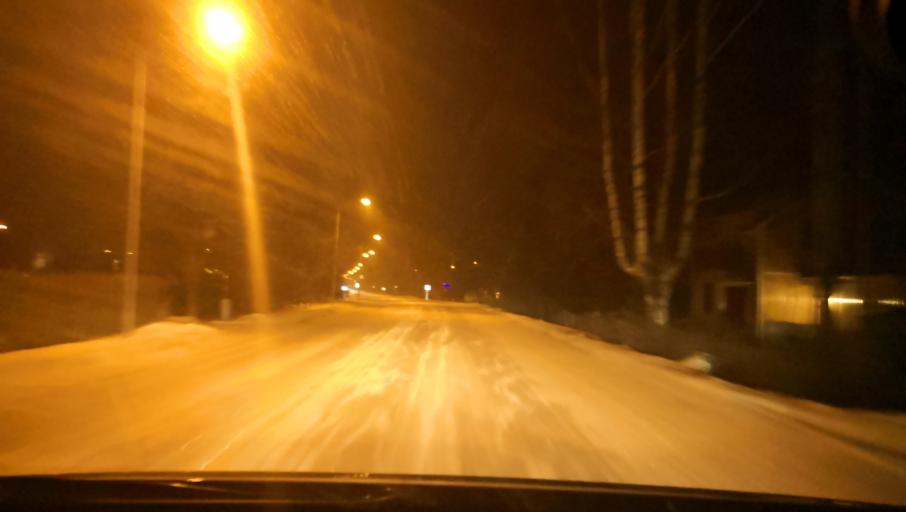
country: SE
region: Uppsala
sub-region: Heby Kommun
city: Tarnsjo
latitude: 60.1519
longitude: 16.9244
